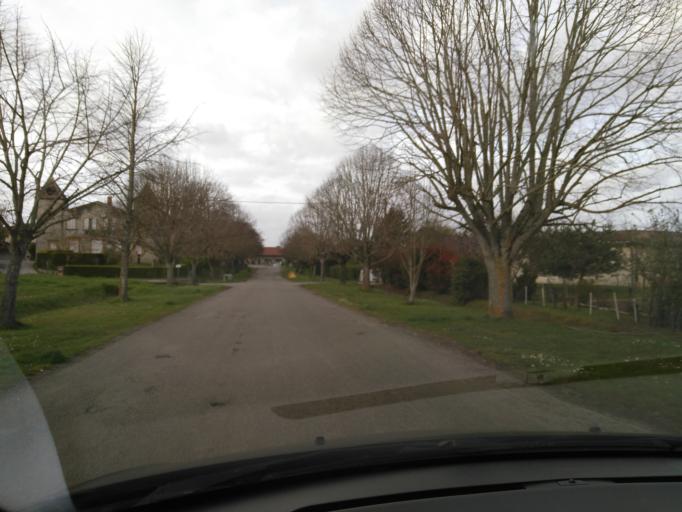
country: FR
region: Midi-Pyrenees
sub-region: Departement du Tarn-et-Garonne
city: Finhan
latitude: 43.8987
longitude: 1.1357
